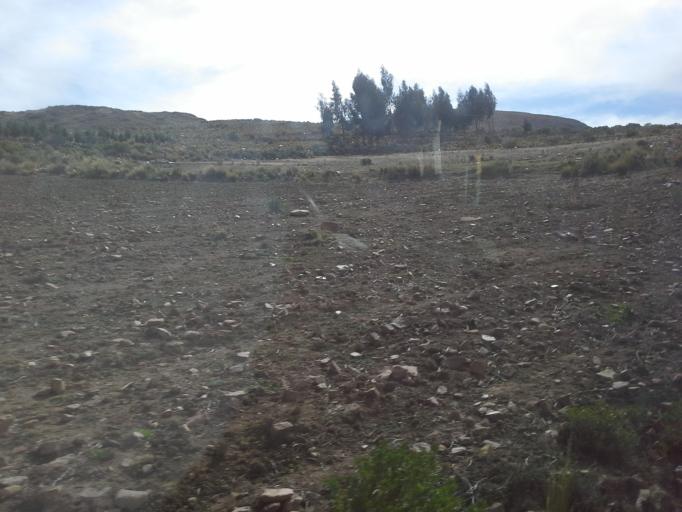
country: BO
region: Cochabamba
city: Colomi
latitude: -17.4381
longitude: -65.8363
